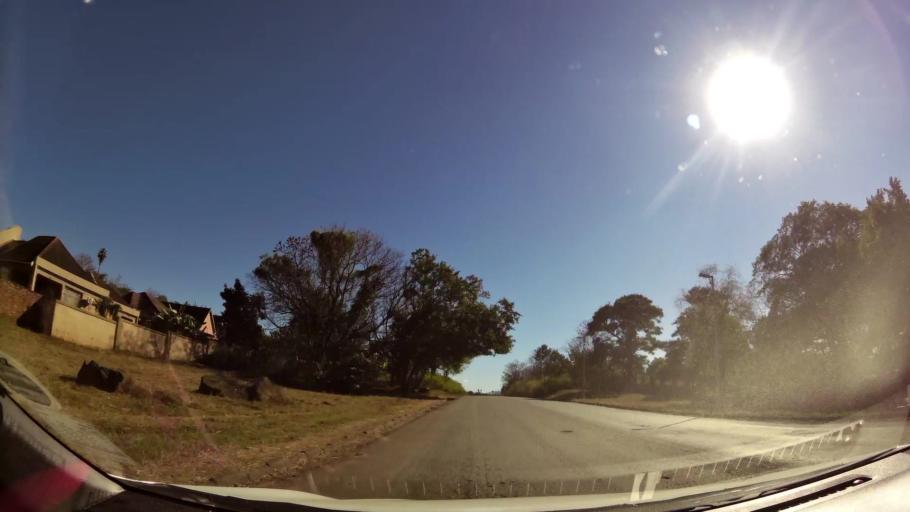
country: ZA
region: Limpopo
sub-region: Mopani District Municipality
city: Tzaneen
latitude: -23.8439
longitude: 30.1672
